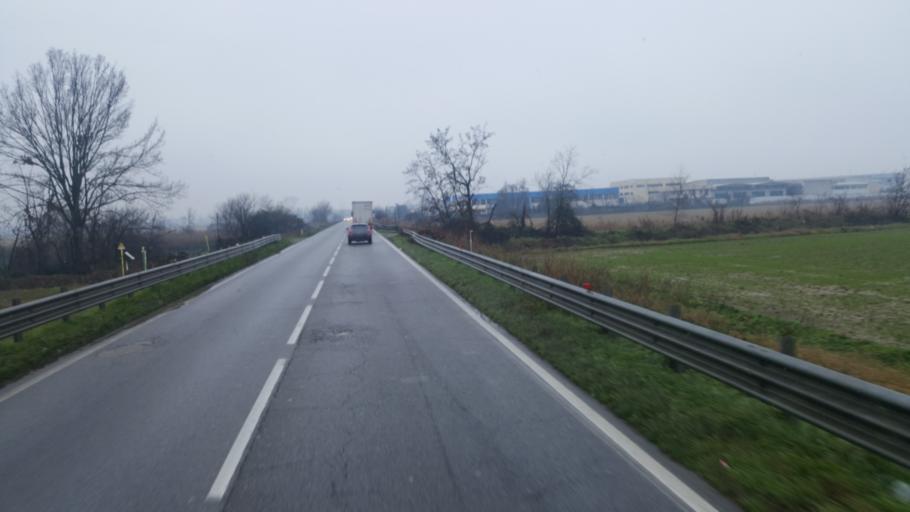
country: IT
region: Lombardy
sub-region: Provincia di Pavia
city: Siziano
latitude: 45.3269
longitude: 9.2215
